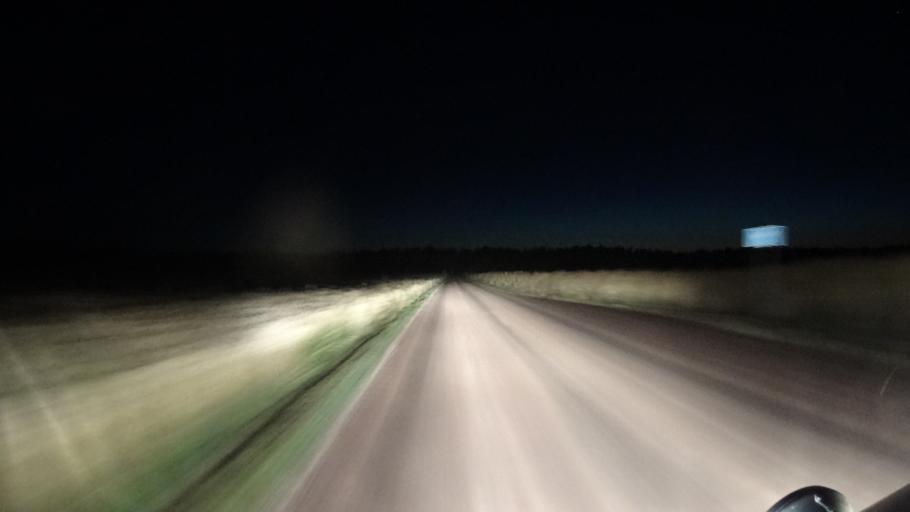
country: SE
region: OEstergoetland
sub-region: Vadstena Kommun
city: Herrestad
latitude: 58.3283
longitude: 14.8243
